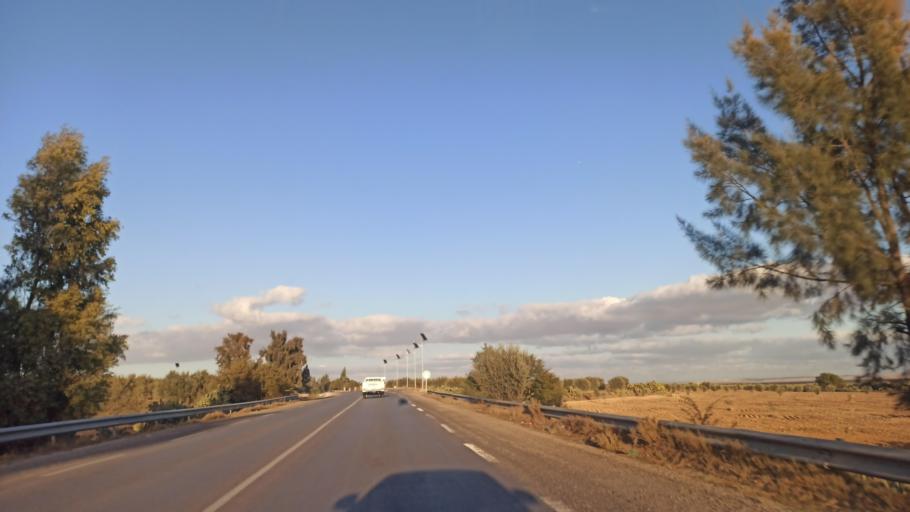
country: TN
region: Al Qayrawan
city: Sbikha
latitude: 35.8541
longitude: 10.1990
